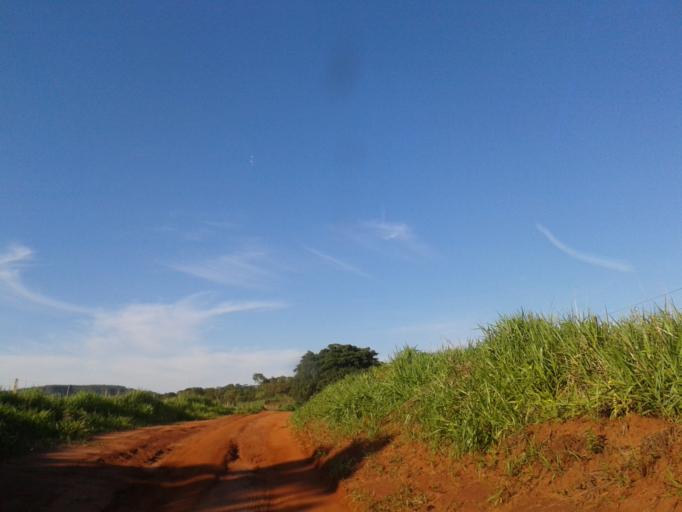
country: BR
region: Minas Gerais
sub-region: Santa Vitoria
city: Santa Vitoria
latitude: -18.9639
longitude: -49.8728
